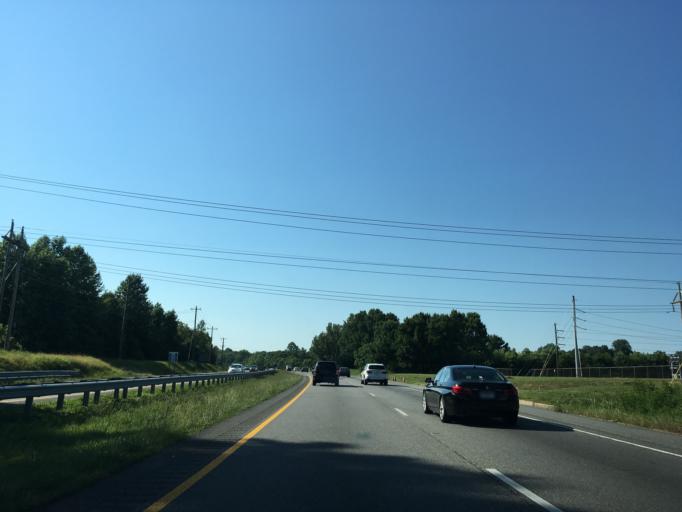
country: US
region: Maryland
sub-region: Queen Anne's County
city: Centreville
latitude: 38.9454
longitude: -76.0634
